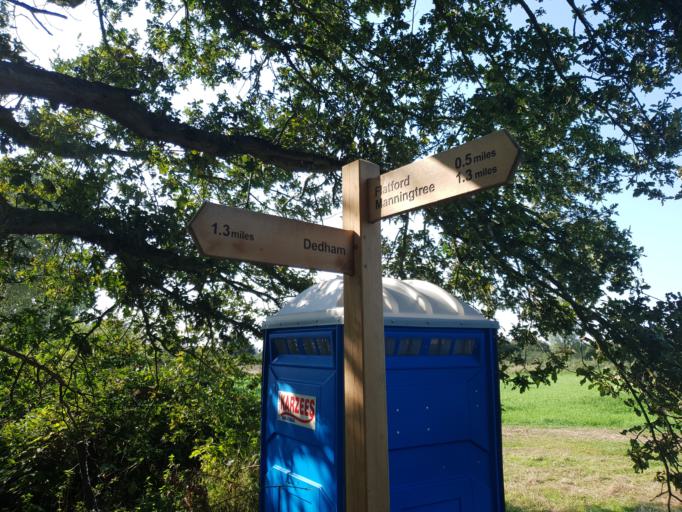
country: GB
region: England
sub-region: Suffolk
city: East Bergholt
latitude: 51.9535
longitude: 1.0216
